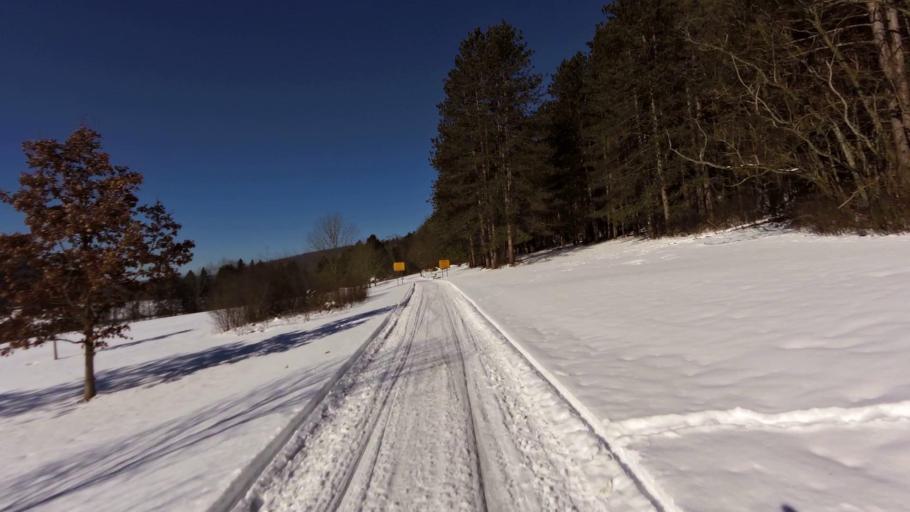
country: US
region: New York
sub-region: Cattaraugus County
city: Salamanca
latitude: 42.1031
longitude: -78.7383
